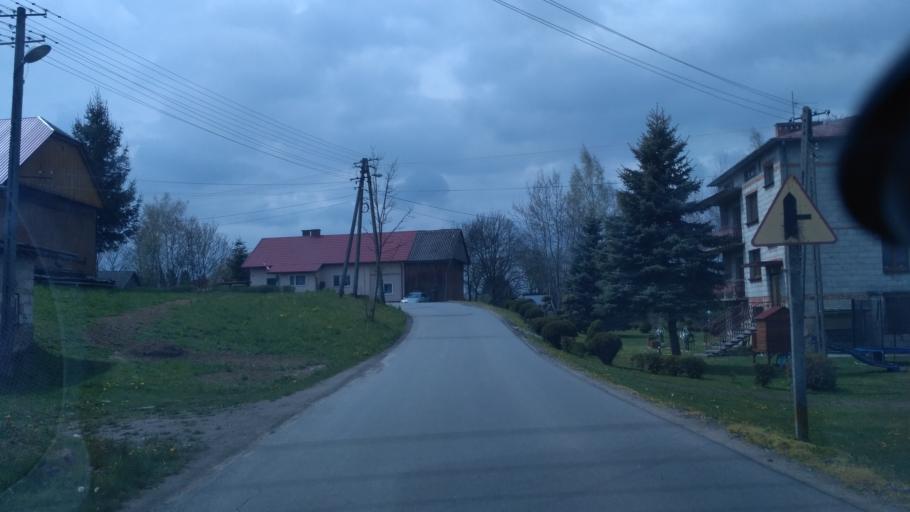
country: PL
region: Subcarpathian Voivodeship
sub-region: Powiat brzozowski
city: Haczow
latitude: 49.6744
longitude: 21.8937
